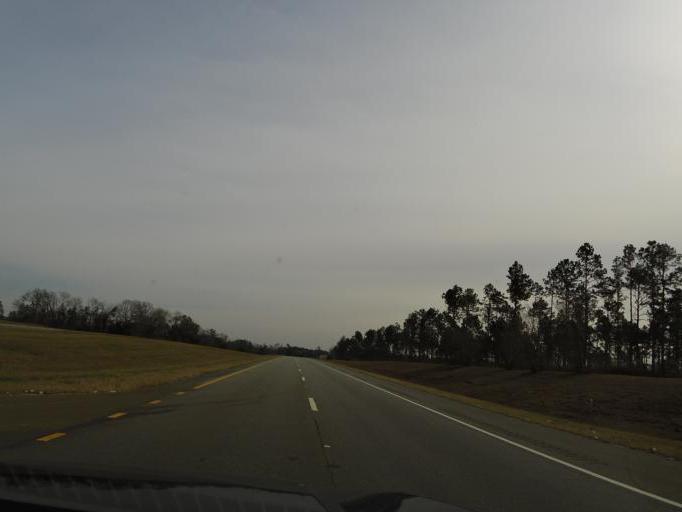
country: US
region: Georgia
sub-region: Seminole County
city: Donalsonville
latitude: 31.1051
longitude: -85.0178
